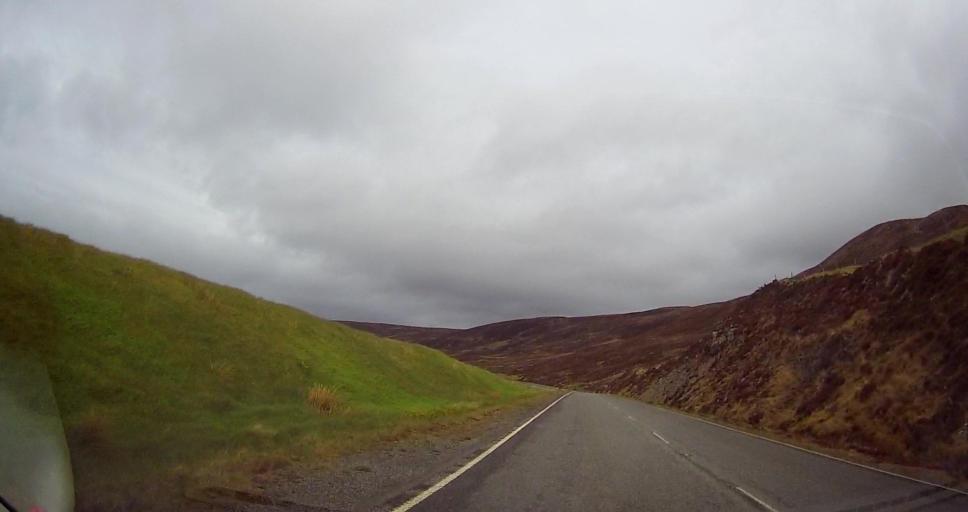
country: GB
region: Scotland
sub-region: Shetland Islands
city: Lerwick
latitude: 60.3595
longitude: -1.2854
